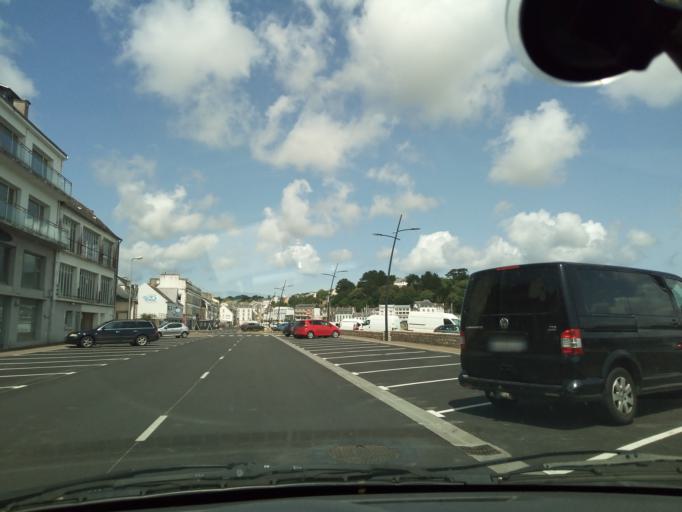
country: FR
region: Brittany
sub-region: Departement du Finistere
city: Audierne
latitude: 48.0202
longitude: -4.5361
